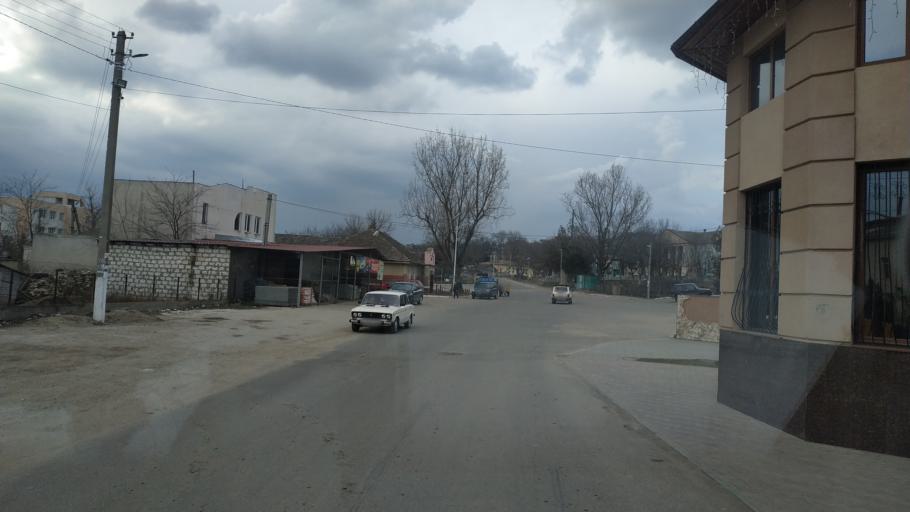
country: MD
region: Anenii Noi
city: Varnita
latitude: 46.8409
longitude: 29.3598
